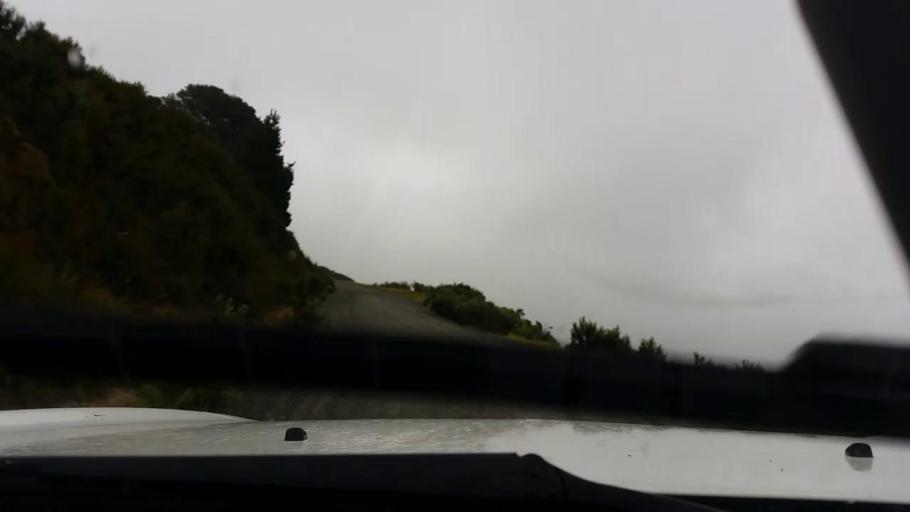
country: NZ
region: Wellington
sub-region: Masterton District
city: Masterton
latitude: -41.2494
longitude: 175.9045
